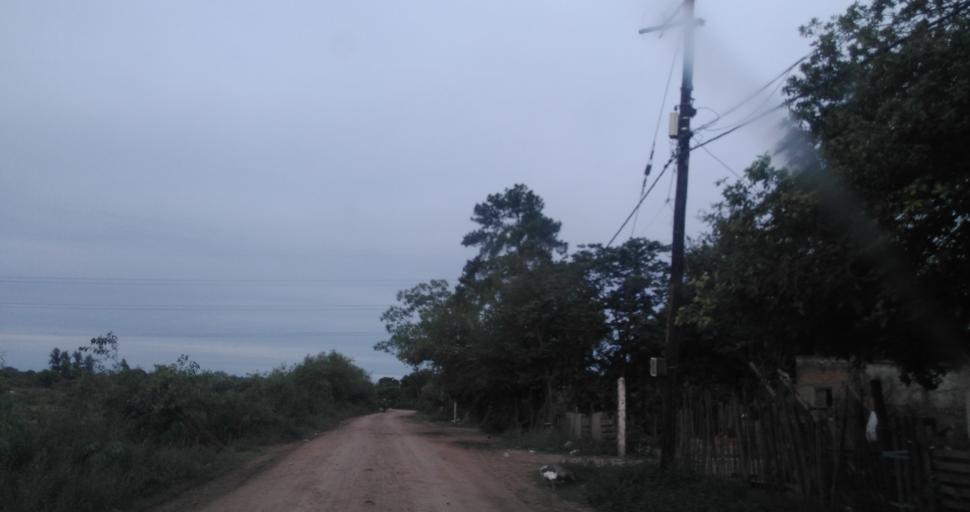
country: AR
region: Chaco
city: Fontana
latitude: -27.4065
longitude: -59.0247
